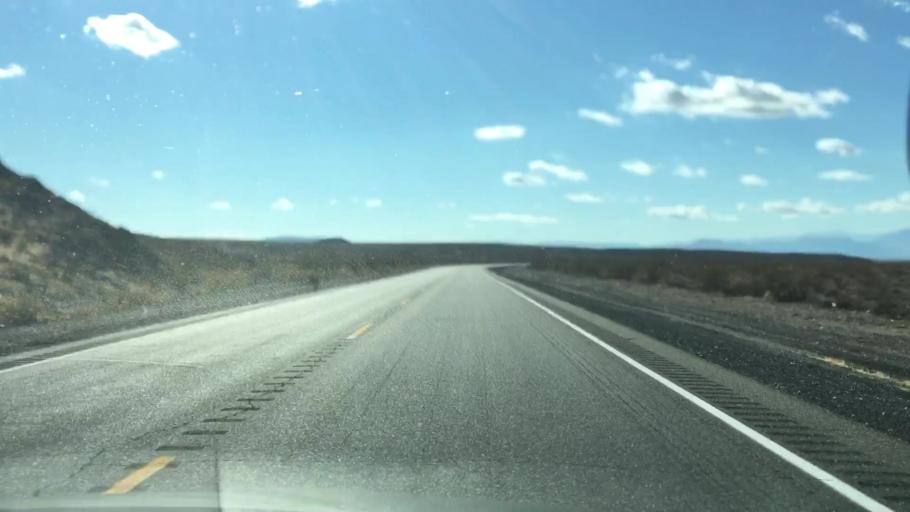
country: US
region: Nevada
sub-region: Nye County
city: Pahrump
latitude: 36.5665
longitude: -116.0825
